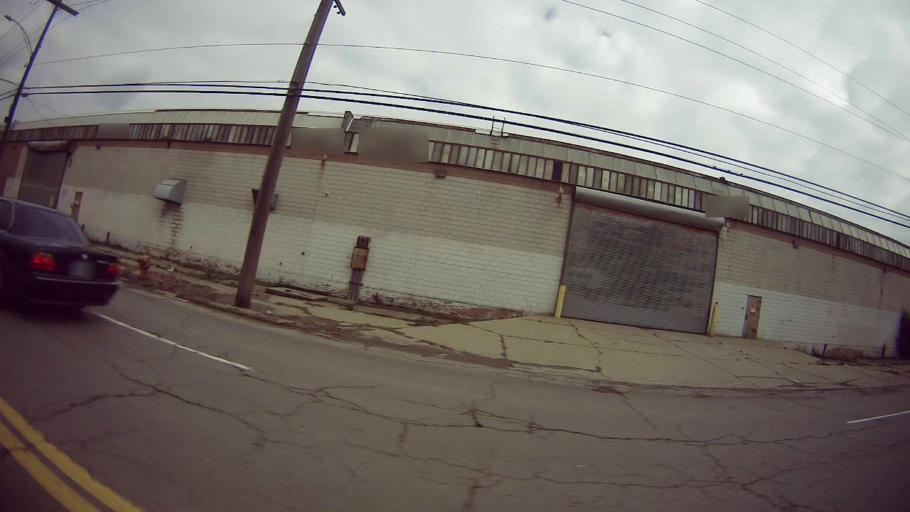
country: US
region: Michigan
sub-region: Wayne County
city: Hamtramck
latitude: 42.4002
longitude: -83.0377
